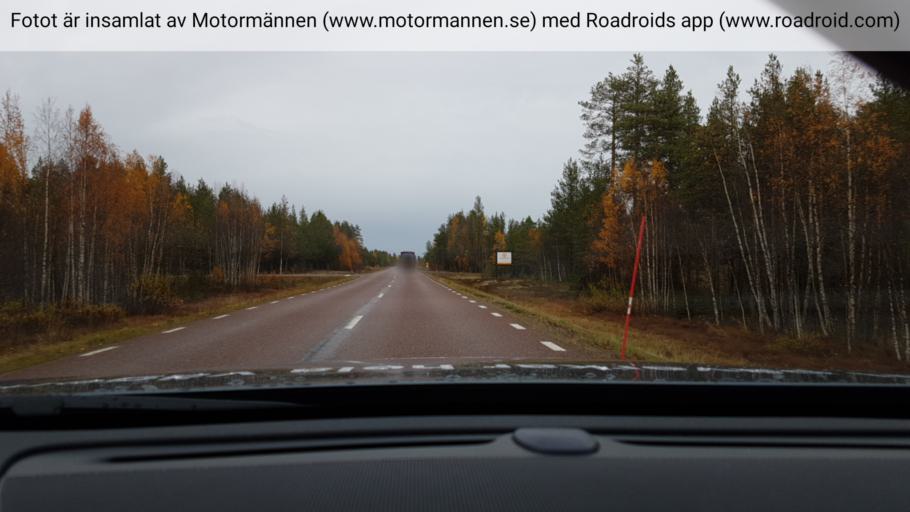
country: SE
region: Norrbotten
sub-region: Pajala Kommun
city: Pajala
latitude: 67.1767
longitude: 22.6950
